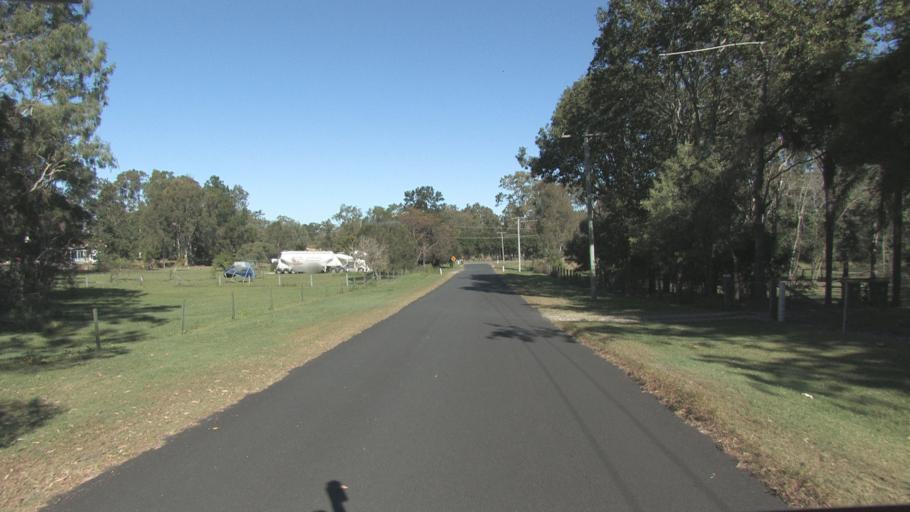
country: AU
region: Queensland
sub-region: Logan
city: Park Ridge South
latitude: -27.7245
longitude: 153.0339
